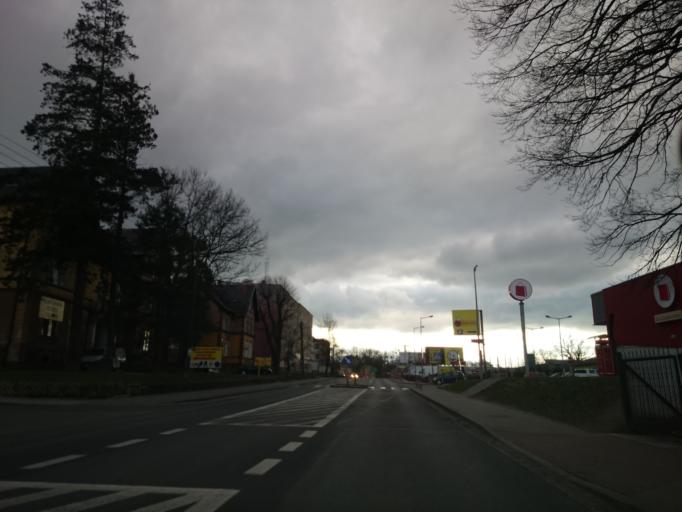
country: PL
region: Opole Voivodeship
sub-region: Powiat opolski
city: Niemodlin
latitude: 50.6412
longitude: 17.6305
